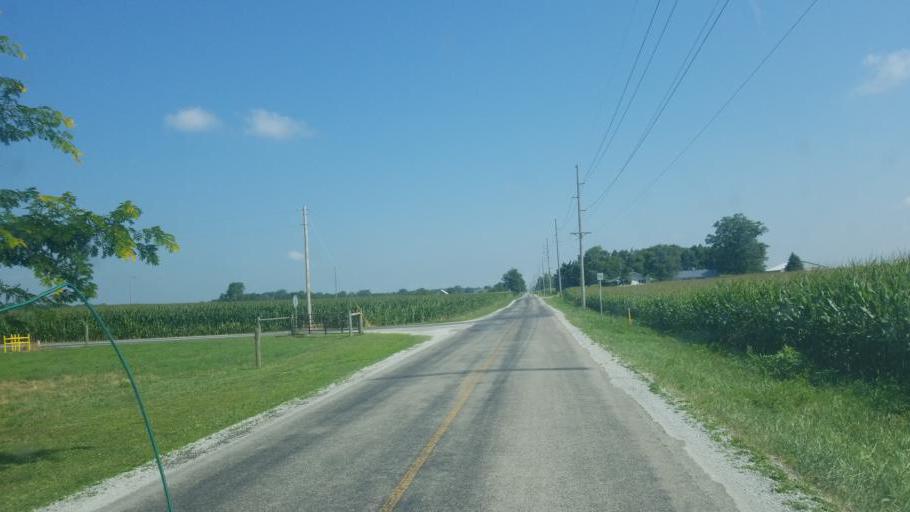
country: US
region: Ohio
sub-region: Hardin County
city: Kenton
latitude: 40.6880
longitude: -83.6540
